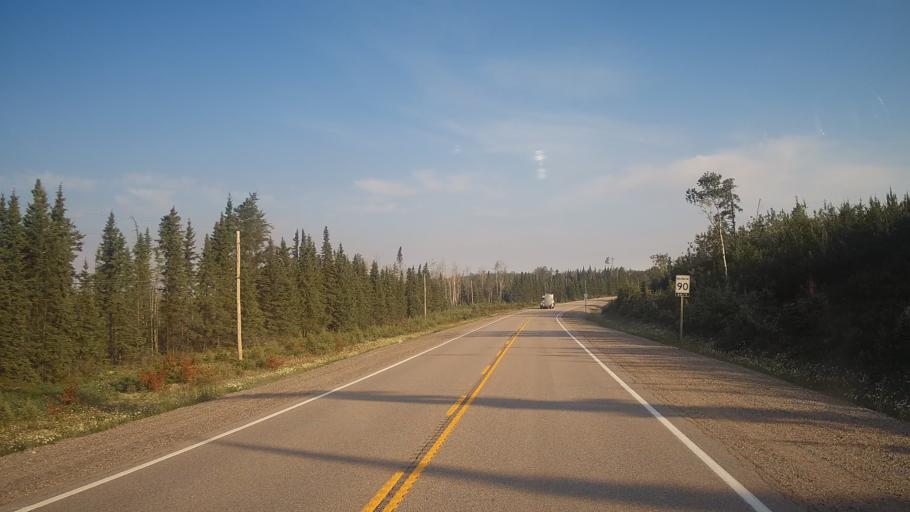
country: CA
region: Ontario
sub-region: Rainy River District
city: Atikokan
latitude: 49.3877
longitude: -91.5977
